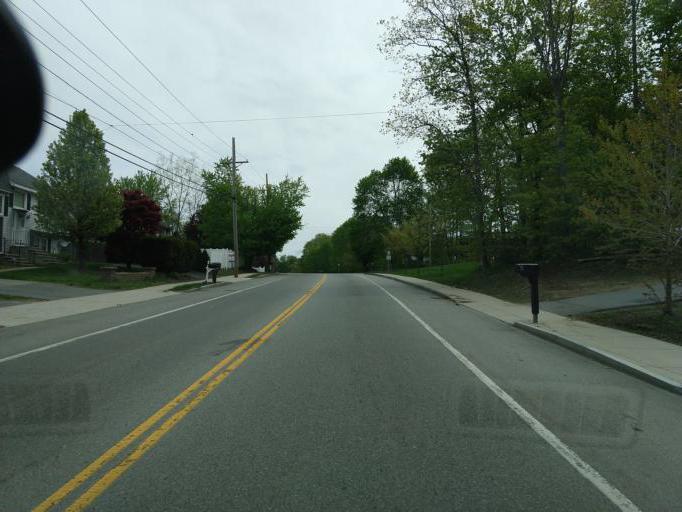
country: US
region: Massachusetts
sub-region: Essex County
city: Haverhill
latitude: 42.7588
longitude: -71.0955
